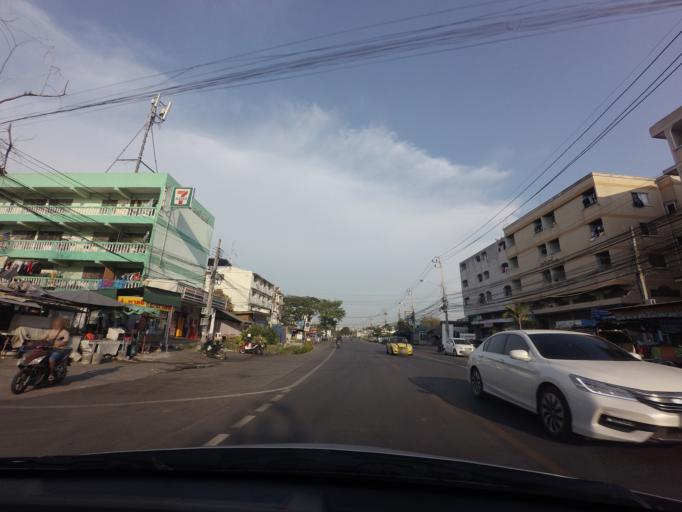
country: TH
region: Bangkok
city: Saphan Sung
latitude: 13.7399
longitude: 100.6891
